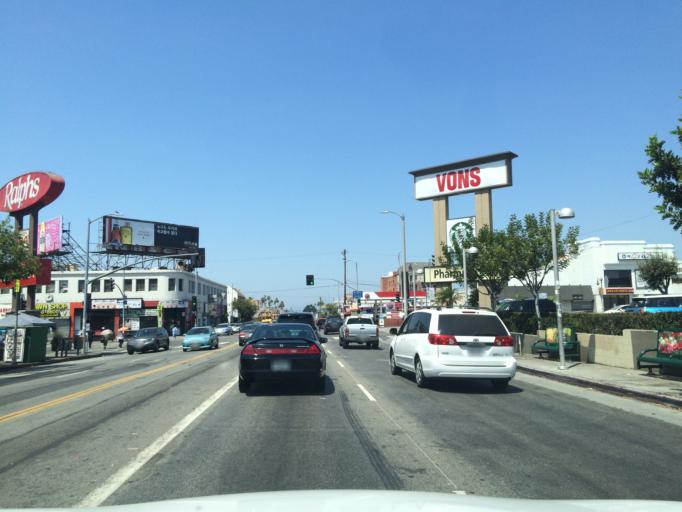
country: US
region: California
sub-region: Los Angeles County
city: Silver Lake
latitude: 34.0691
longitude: -118.2910
